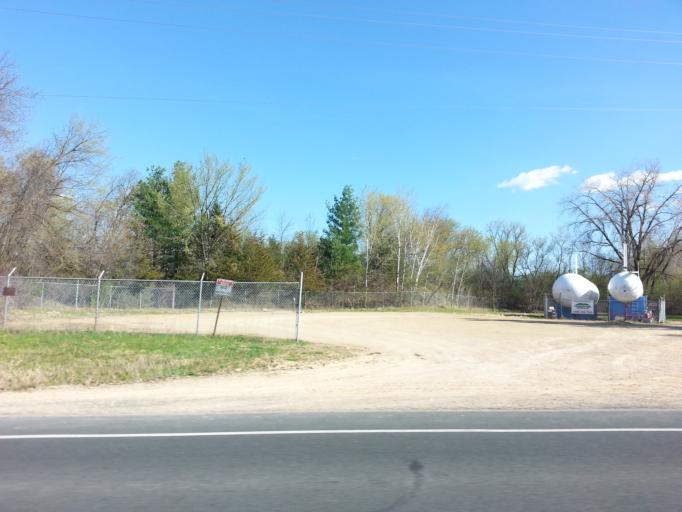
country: US
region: Wisconsin
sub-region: Saint Croix County
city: North Hudson
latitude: 45.0187
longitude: -92.6704
